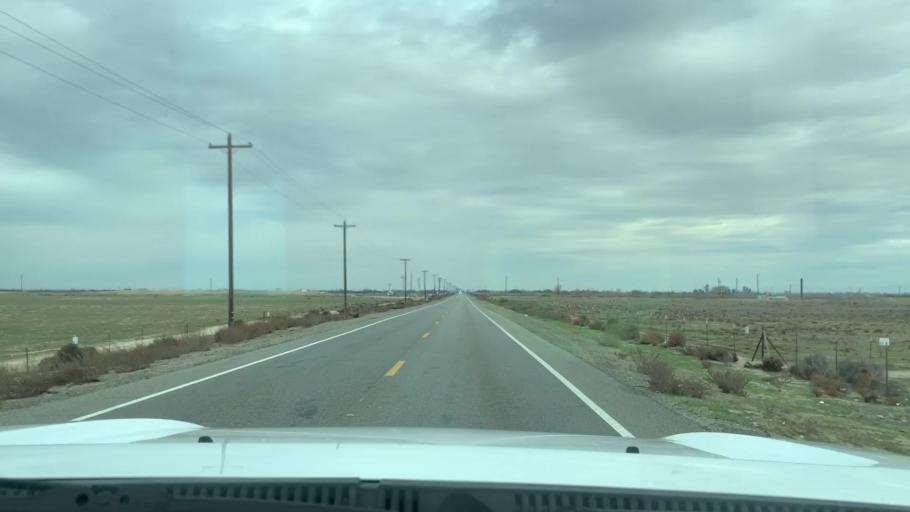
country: US
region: California
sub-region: Kern County
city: Rosedale
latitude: 35.3070
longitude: -119.2524
